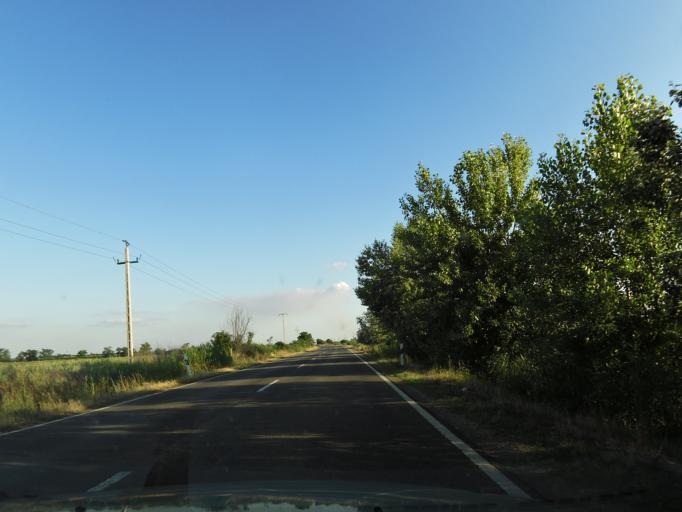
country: HU
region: Jasz-Nagykun-Szolnok
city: Tiszafoldvar
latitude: 46.9245
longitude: 20.2672
